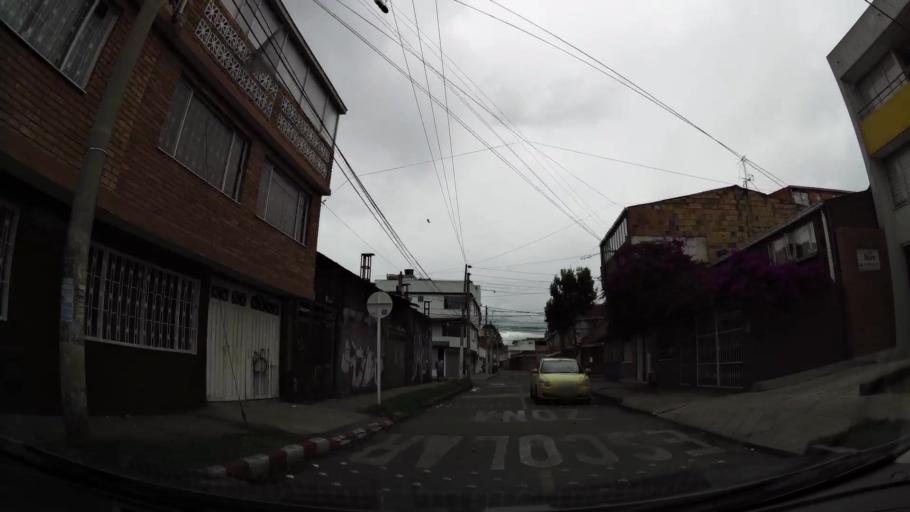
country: CO
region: Bogota D.C.
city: Bogota
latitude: 4.6783
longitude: -74.0971
